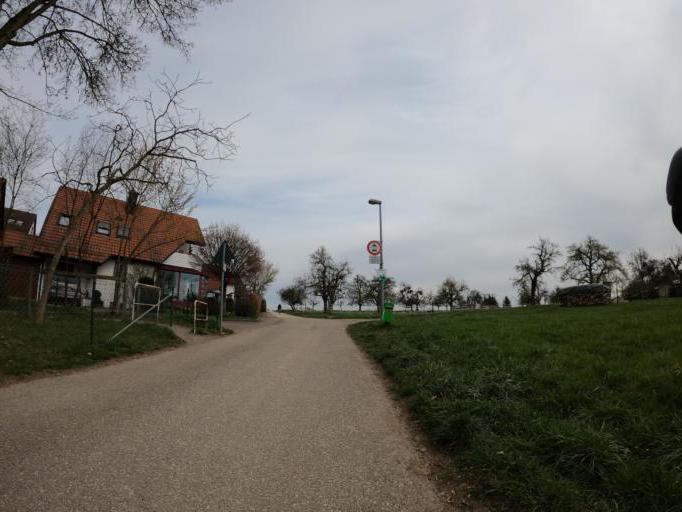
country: DE
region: Baden-Wuerttemberg
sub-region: Regierungsbezirk Stuttgart
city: Filderstadt
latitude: 48.6469
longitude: 9.2225
